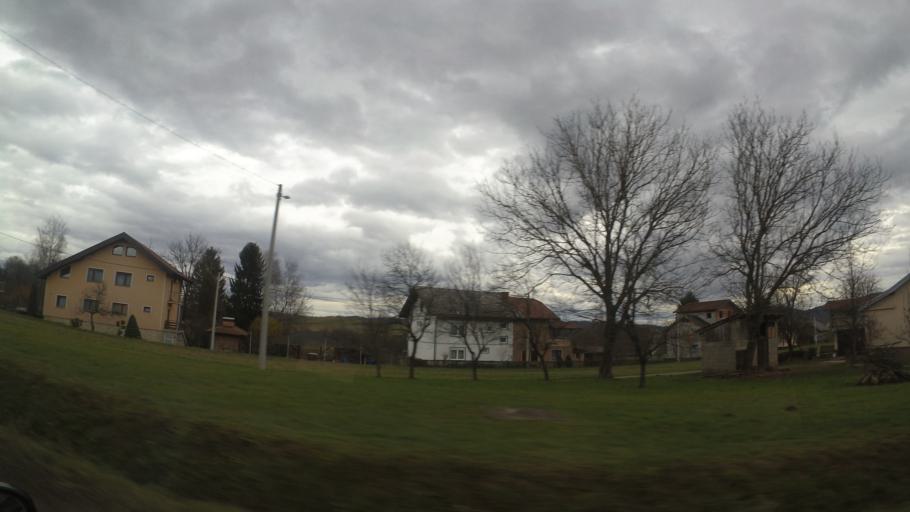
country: HR
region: Karlovacka
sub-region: Grad Karlovac
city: Karlovac
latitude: 45.4441
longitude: 15.5545
